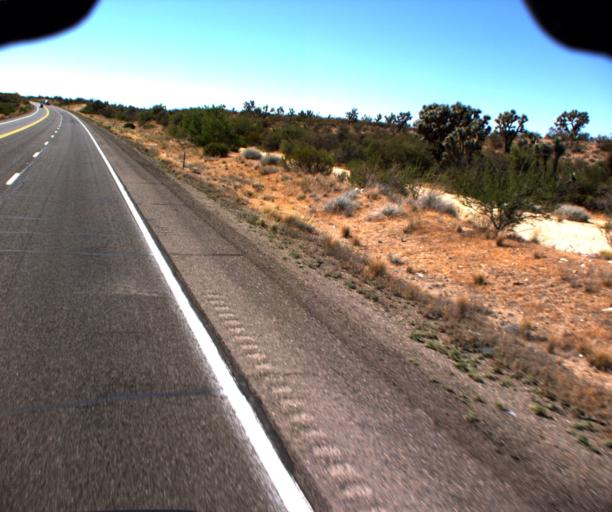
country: US
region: Arizona
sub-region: Yavapai County
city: Congress
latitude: 34.1981
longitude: -113.0598
